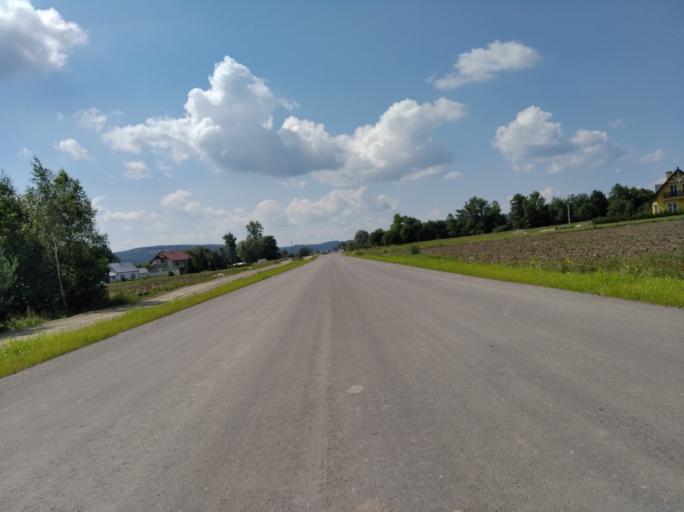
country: PL
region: Subcarpathian Voivodeship
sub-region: Powiat rzeszowski
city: Dynow
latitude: 49.8295
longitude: 22.2416
